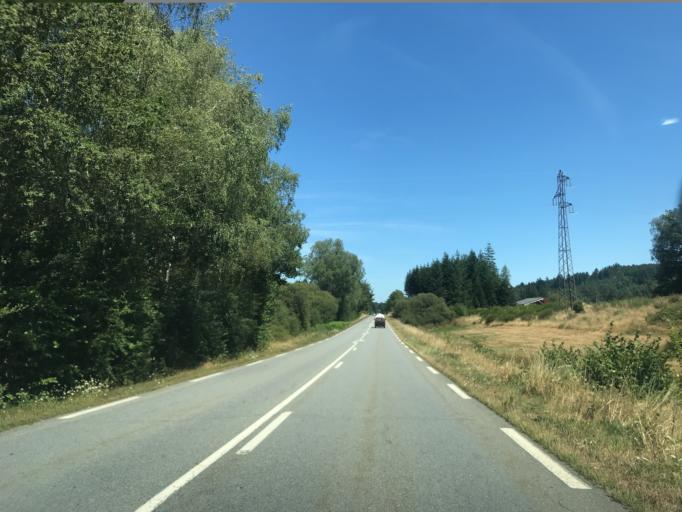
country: FR
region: Limousin
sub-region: Departement de la Correze
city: Meymac
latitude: 45.4926
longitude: 2.2117
